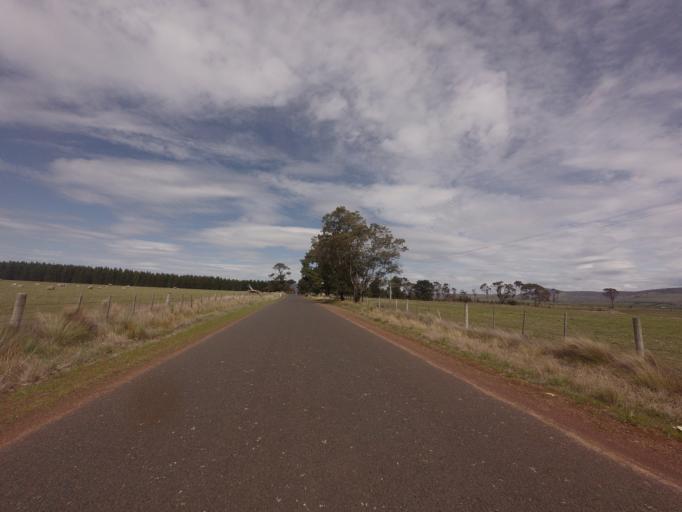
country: AU
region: Tasmania
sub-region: Northern Midlands
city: Evandale
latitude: -41.8606
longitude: 147.3459
